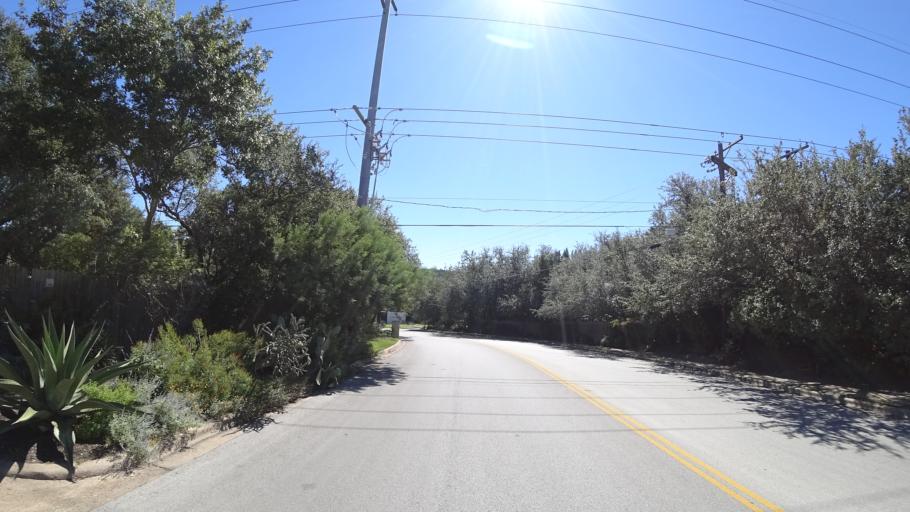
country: US
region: Texas
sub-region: Travis County
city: West Lake Hills
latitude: 30.3398
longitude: -97.7785
